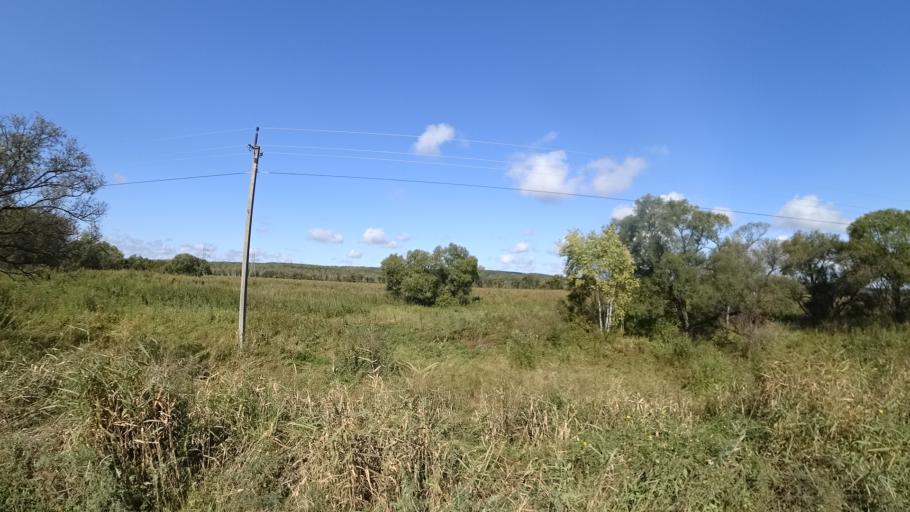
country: RU
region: Amur
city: Arkhara
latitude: 49.4106
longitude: 130.1642
